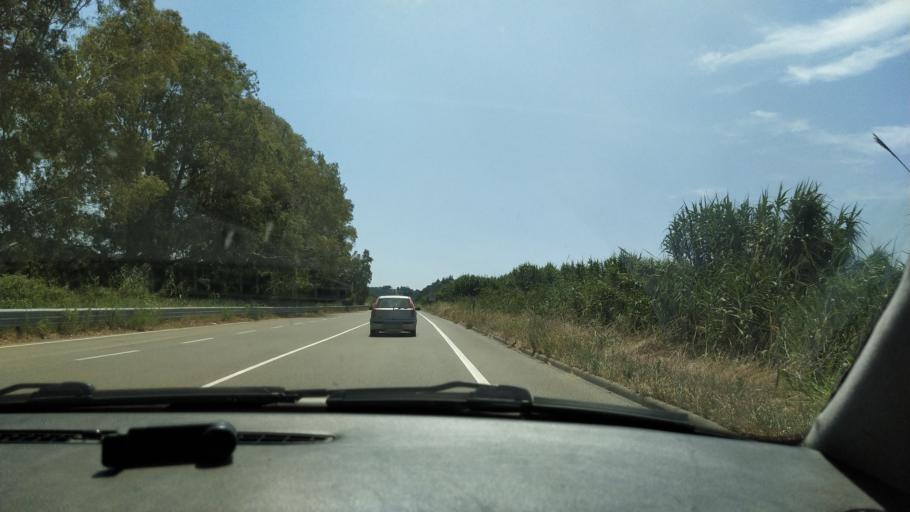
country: IT
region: Apulia
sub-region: Provincia di Taranto
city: Marina di Ginosa
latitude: 40.4366
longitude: 16.7873
